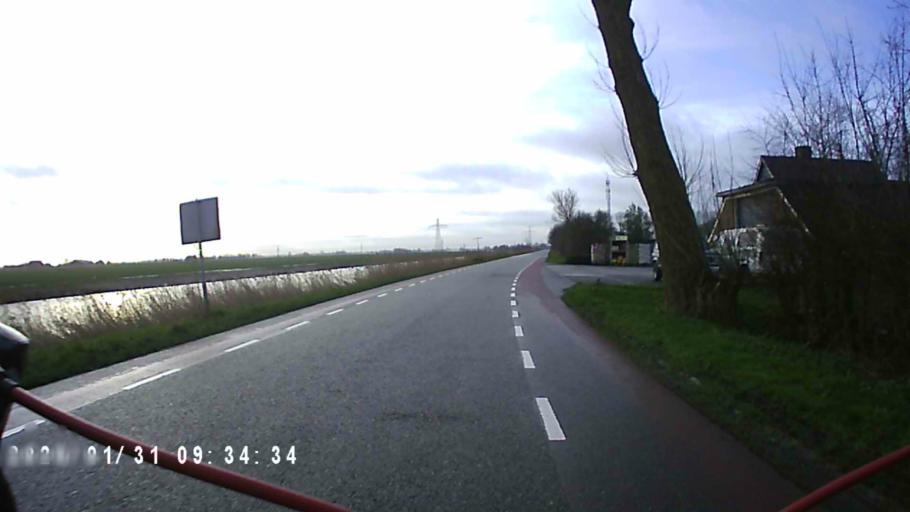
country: NL
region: Groningen
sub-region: Gemeente Winsum
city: Winsum
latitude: 53.3060
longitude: 6.4801
